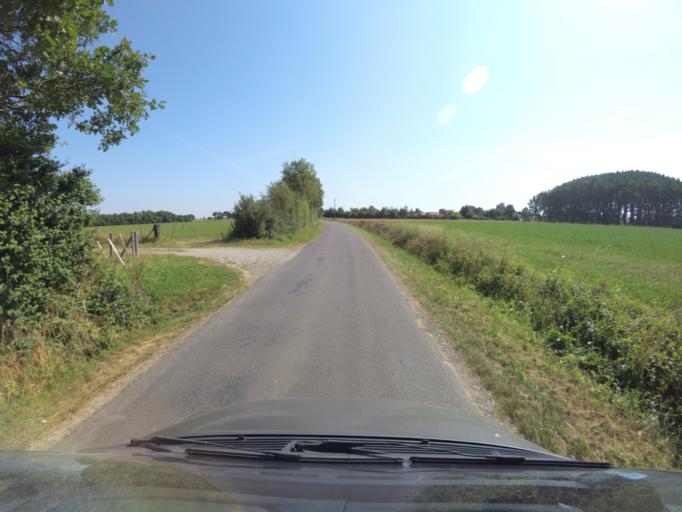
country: FR
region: Pays de la Loire
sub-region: Departement de la Loire-Atlantique
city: Vieillevigne
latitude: 46.9860
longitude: -1.4645
